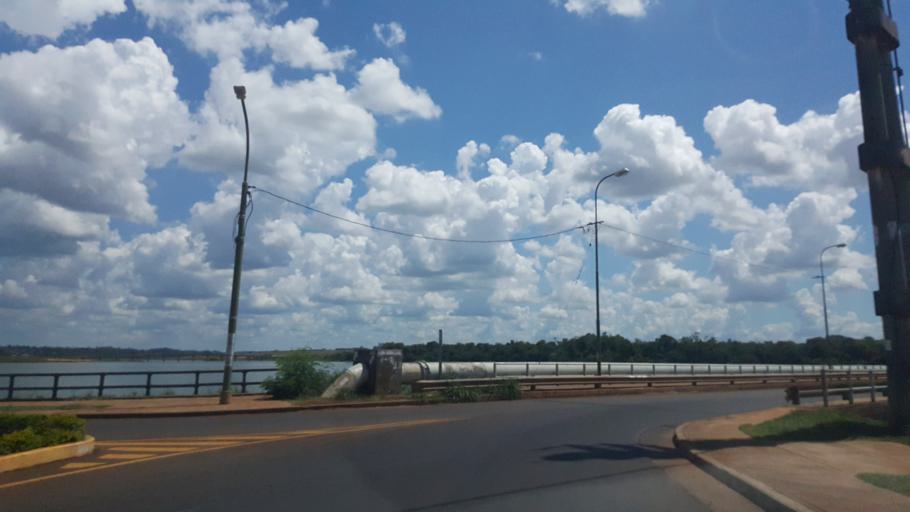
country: AR
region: Misiones
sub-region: Departamento de Capital
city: Posadas
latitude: -27.3716
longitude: -55.9542
